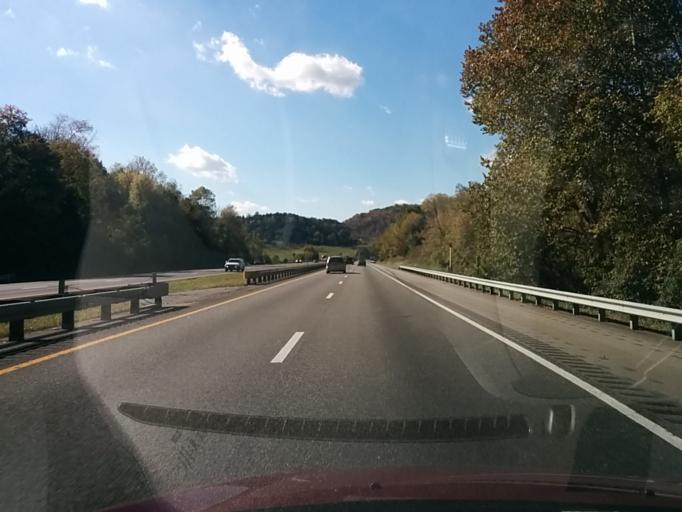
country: US
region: Virginia
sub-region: Botetourt County
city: Buchanan
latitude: 37.5046
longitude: -79.7456
